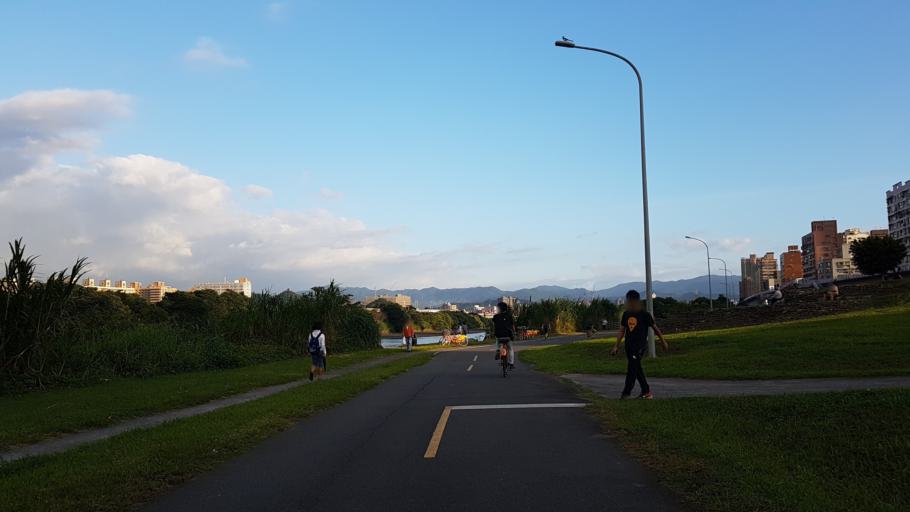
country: TW
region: Taipei
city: Taipei
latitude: 25.0176
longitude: 121.5197
